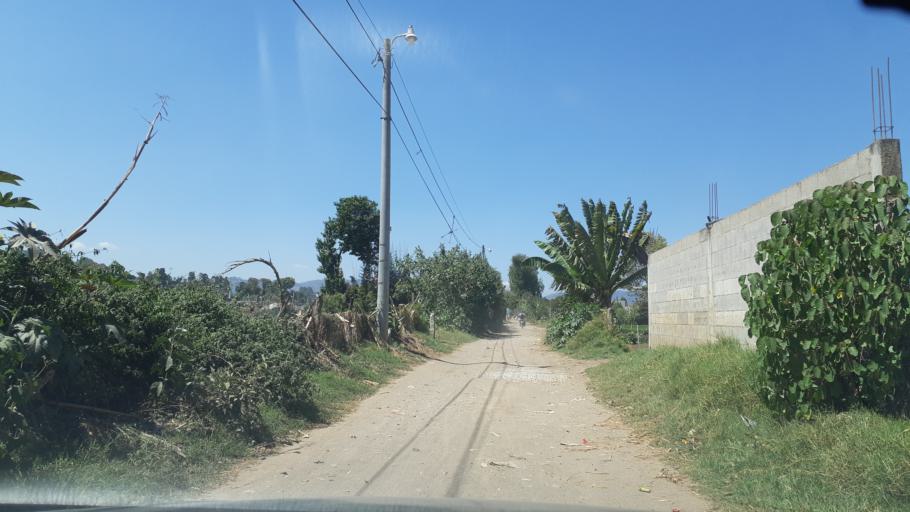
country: GT
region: Chimaltenango
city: El Tejar
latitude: 14.6448
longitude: -90.8081
